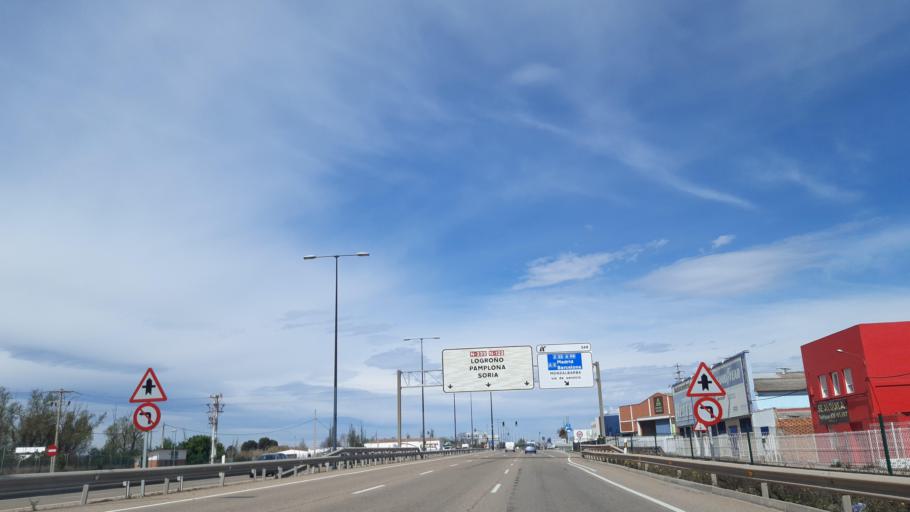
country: ES
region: Aragon
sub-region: Provincia de Zaragoza
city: Utebo
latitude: 41.6877
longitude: -0.9756
